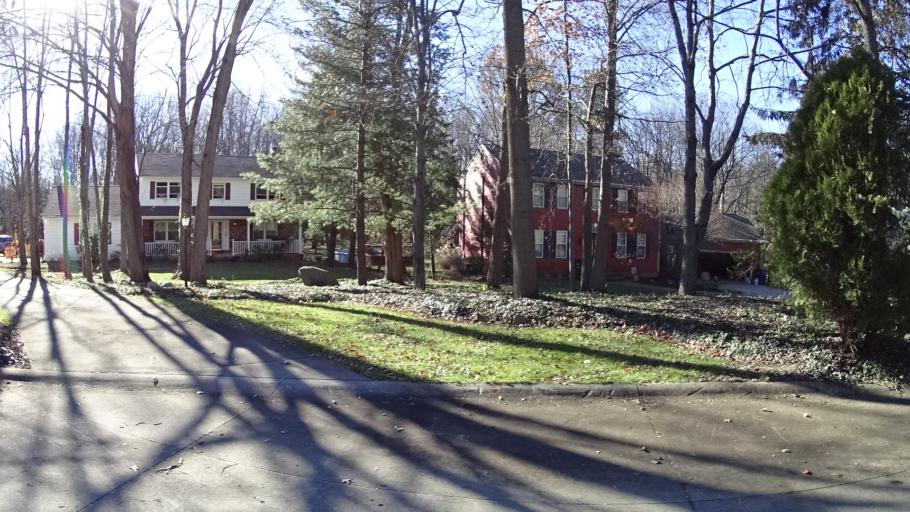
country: US
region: Ohio
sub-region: Lorain County
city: Elyria
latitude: 41.3356
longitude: -82.0829
